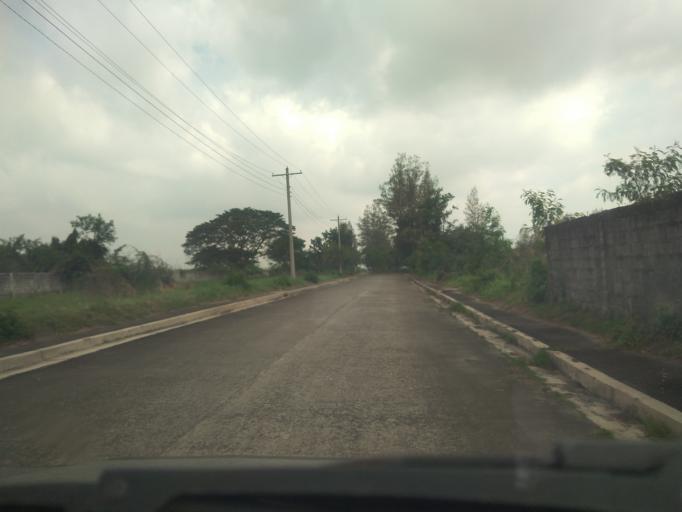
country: PH
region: Central Luzon
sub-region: Province of Pampanga
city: Santo Domingo
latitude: 15.0031
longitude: 120.7235
